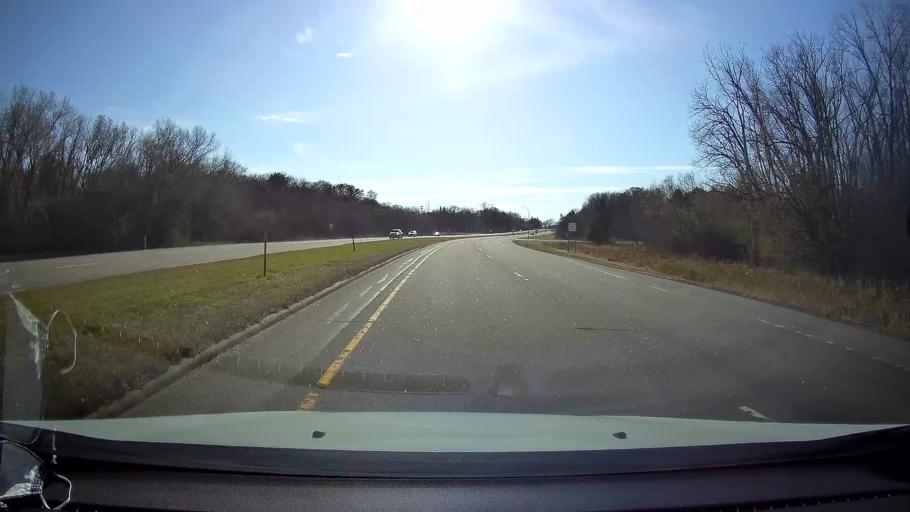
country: US
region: Minnesota
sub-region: Ramsey County
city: Arden Hills
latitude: 45.0402
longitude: -93.1584
